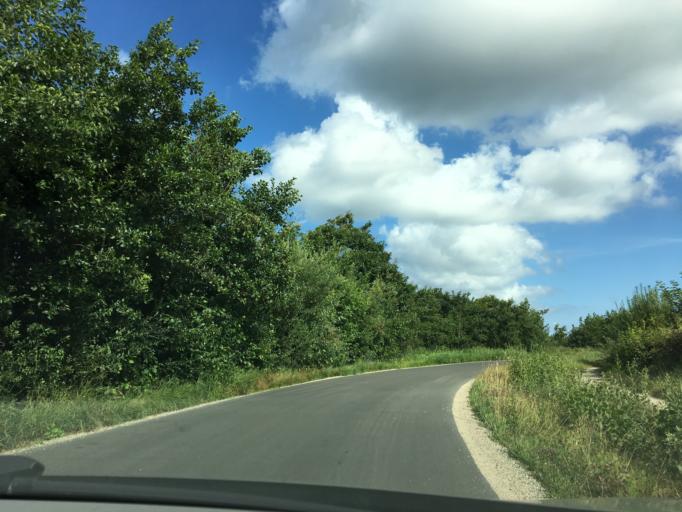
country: DK
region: South Denmark
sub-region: Varde Kommune
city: Oksbol
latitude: 55.8381
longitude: 8.2678
